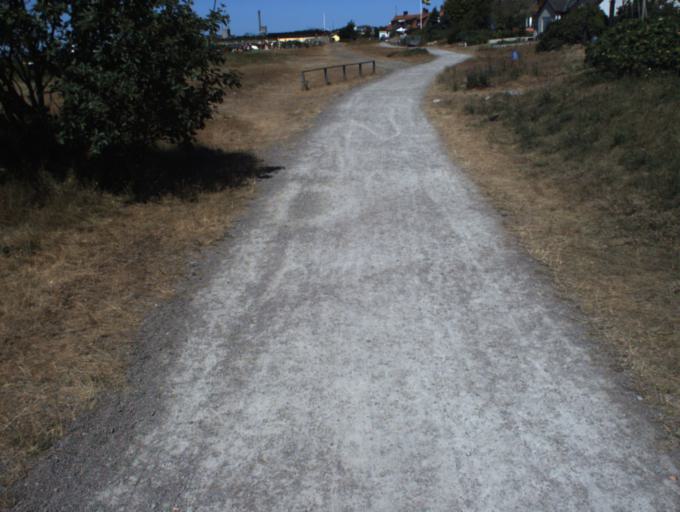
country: SE
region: Skane
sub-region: Helsingborg
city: Rydeback
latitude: 55.9940
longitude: 12.7425
